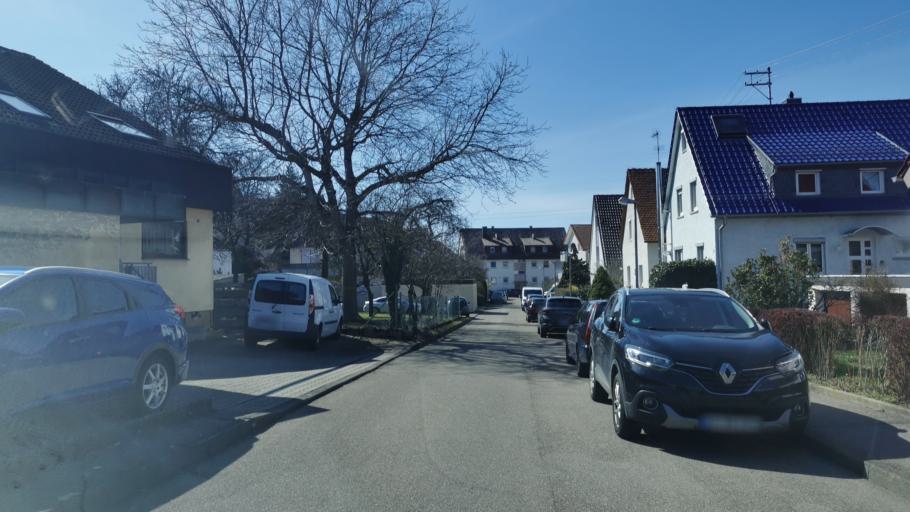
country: DE
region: Baden-Wuerttemberg
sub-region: Regierungsbezirk Stuttgart
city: Rutesheim
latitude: 48.8080
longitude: 8.9504
